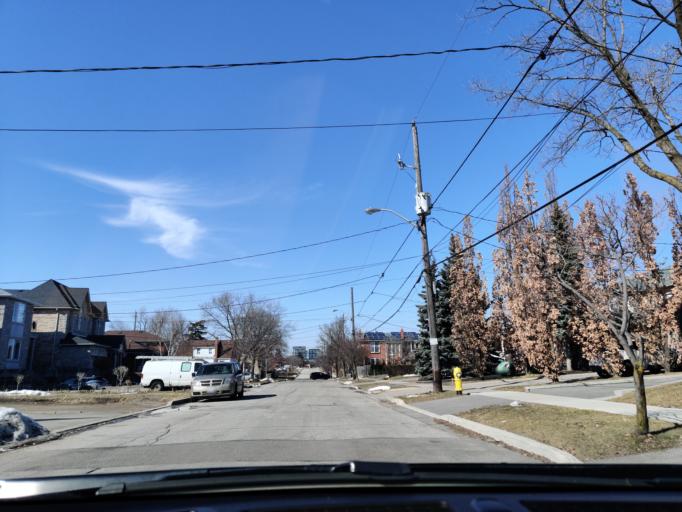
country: CA
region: Ontario
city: Toronto
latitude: 43.7175
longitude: -79.4773
